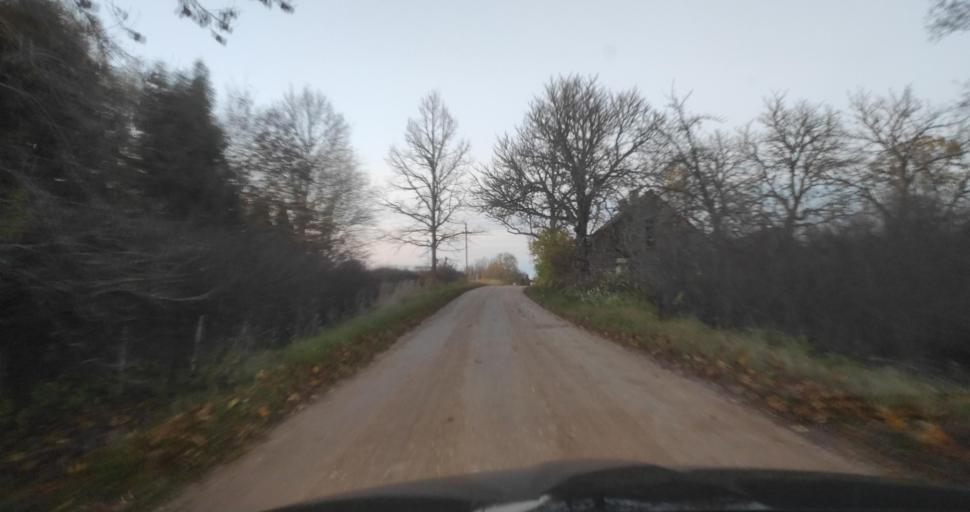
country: LV
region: Saldus Rajons
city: Saldus
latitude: 56.8039
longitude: 22.2849
